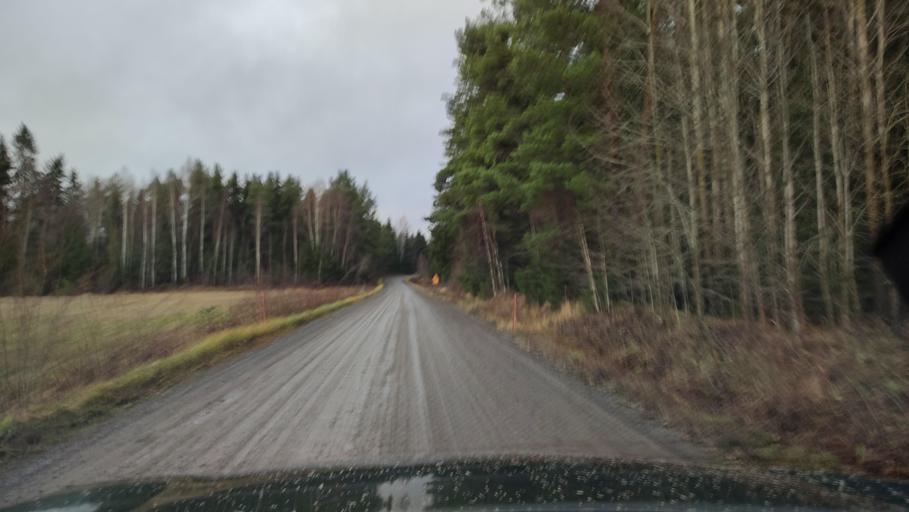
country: FI
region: Ostrobothnia
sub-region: Sydosterbotten
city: Naerpes
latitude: 62.4605
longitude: 21.4911
